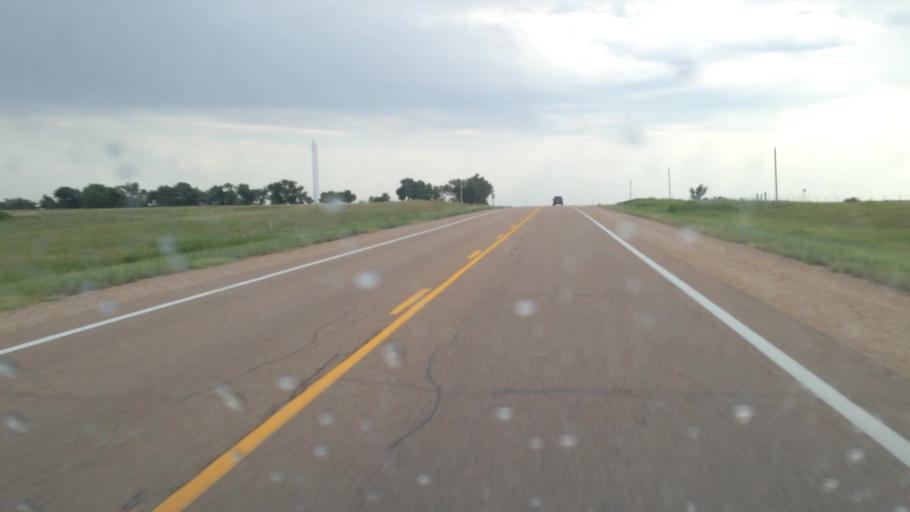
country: US
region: Kansas
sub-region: Coffey County
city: Burlington
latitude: 38.1443
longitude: -95.7392
